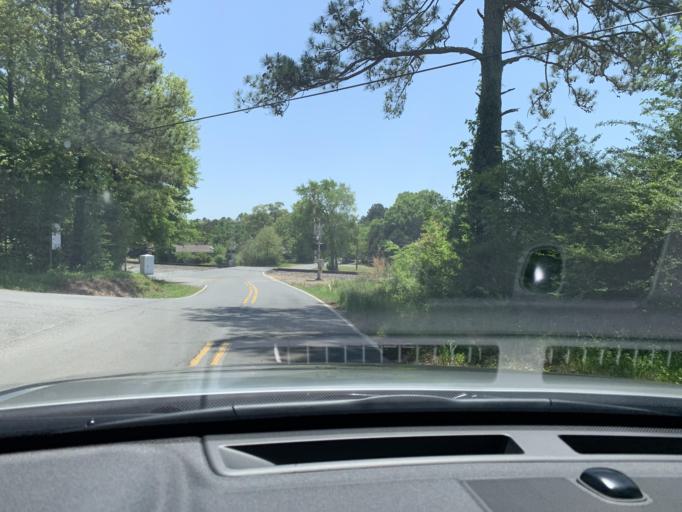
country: US
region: Georgia
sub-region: Polk County
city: Aragon
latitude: 34.0872
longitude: -85.1240
